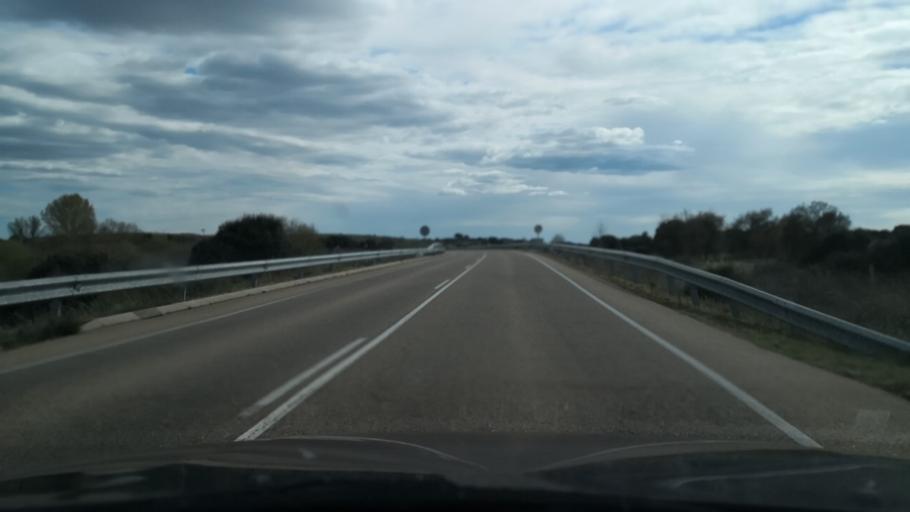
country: ES
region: Castille and Leon
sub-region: Provincia de Salamanca
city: Herguijuela de Ciudad Rodrigo
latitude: 40.4889
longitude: -6.5819
